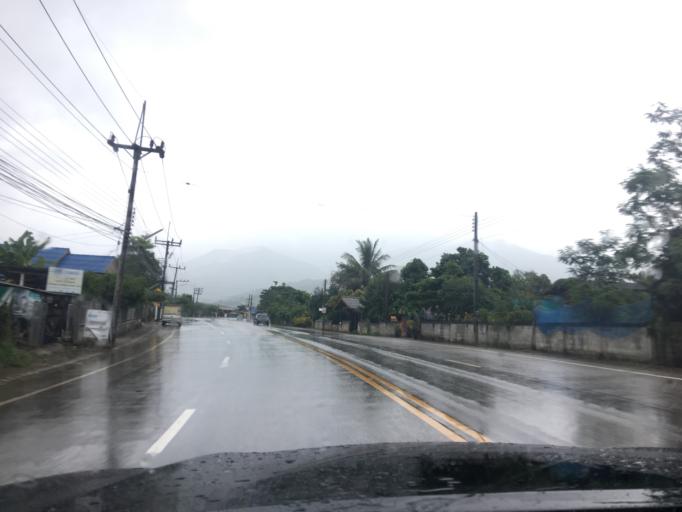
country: TH
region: Chiang Rai
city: Chiang Khong
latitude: 20.3009
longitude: 100.2491
